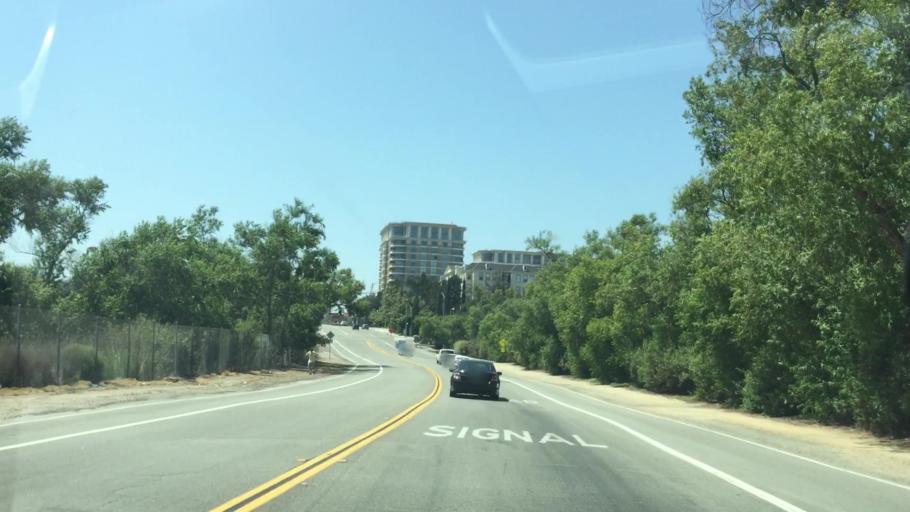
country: US
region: California
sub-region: Orange County
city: Irvine
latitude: 33.6627
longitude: -117.8497
